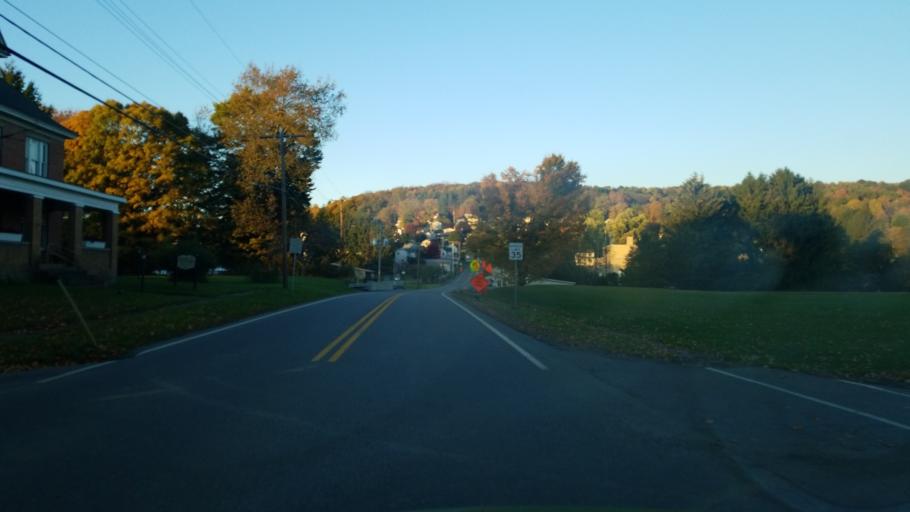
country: US
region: Pennsylvania
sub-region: Jefferson County
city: Reynoldsville
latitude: 41.0883
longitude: -78.8872
